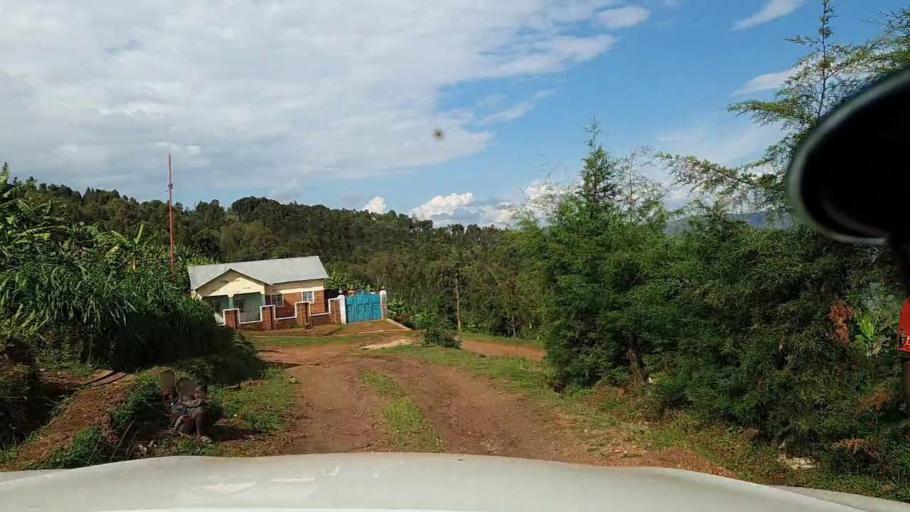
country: RW
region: Kigali
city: Kigali
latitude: -1.7901
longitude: 29.8421
